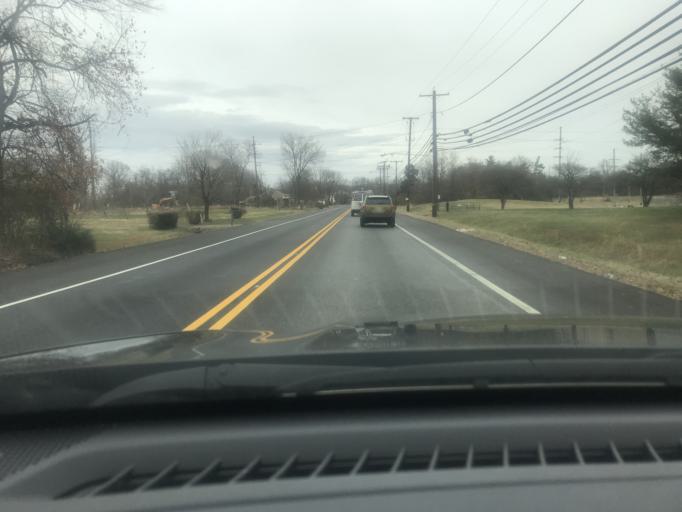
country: US
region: Maryland
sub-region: Prince George's County
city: Friendly
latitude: 38.7735
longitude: -76.9612
